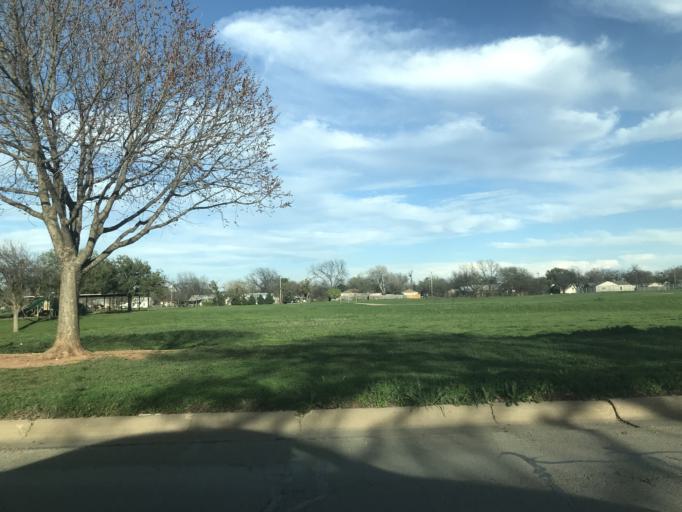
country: US
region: Texas
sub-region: Taylor County
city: Abilene
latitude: 32.4357
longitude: -99.7642
